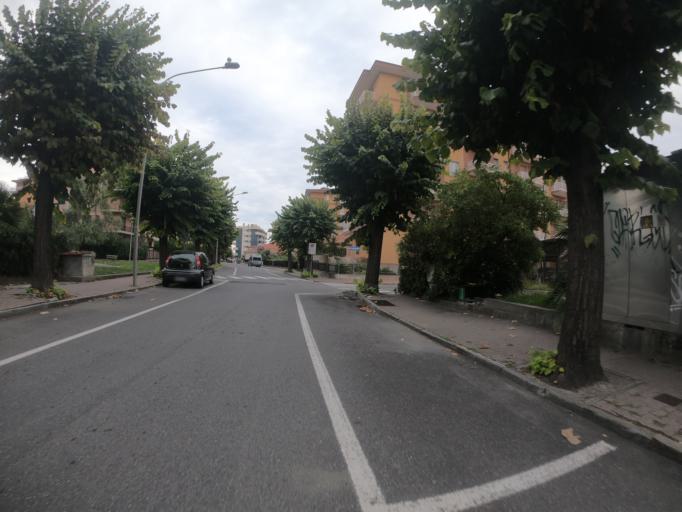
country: IT
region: Liguria
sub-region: Provincia di Savona
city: Marina di Andora
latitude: 43.9532
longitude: 8.1480
